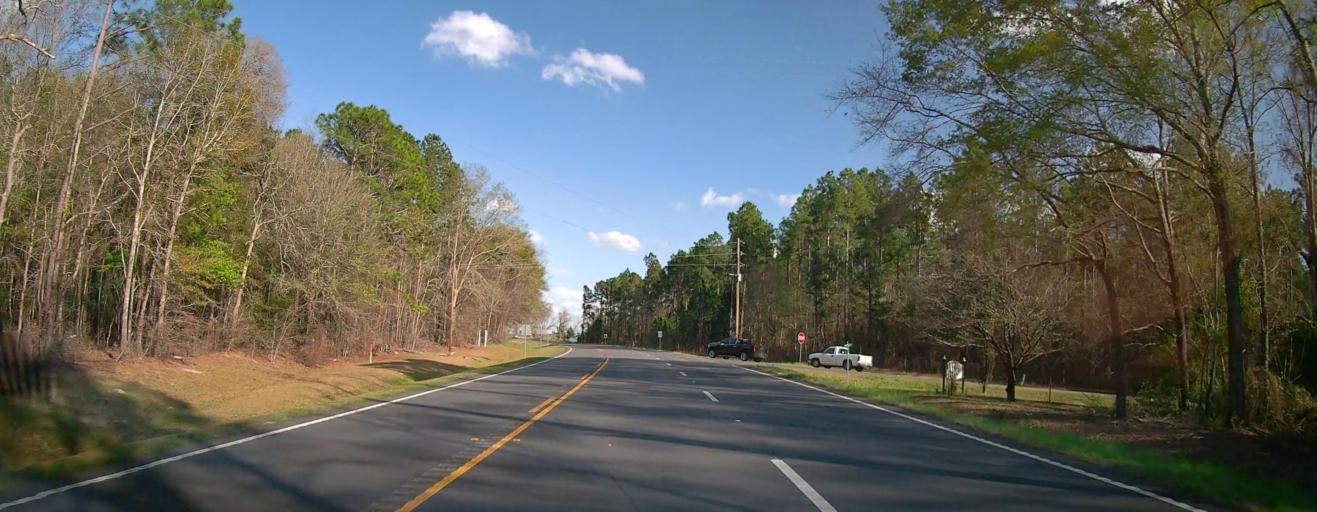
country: US
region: Georgia
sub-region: Montgomery County
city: Mount Vernon
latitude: 32.1806
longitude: -82.5569
